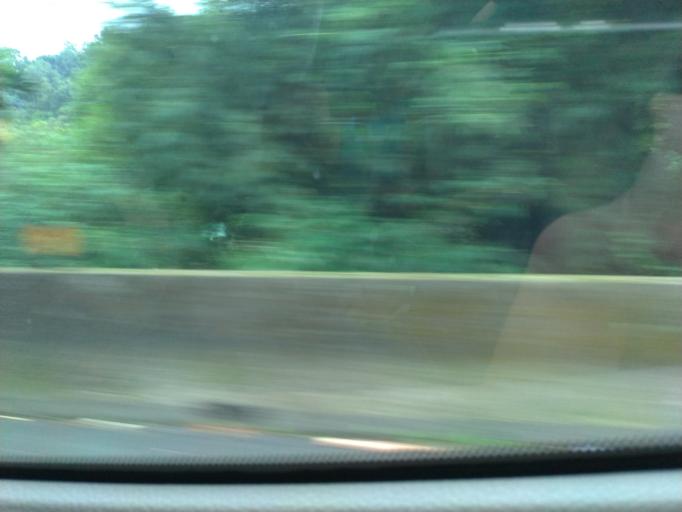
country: TW
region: Taipei
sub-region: Taipei
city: Banqiao
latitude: 24.9283
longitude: 121.4238
